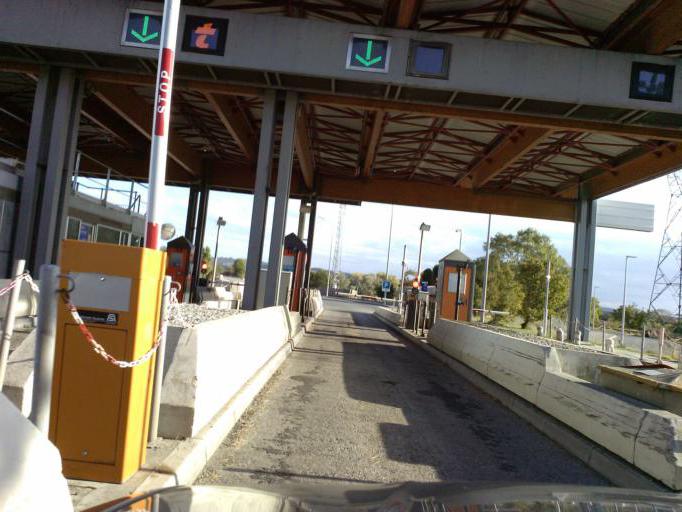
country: FR
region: Provence-Alpes-Cote d'Azur
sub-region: Departement des Alpes-de-Haute-Provence
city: Manosque
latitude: 43.8080
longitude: 5.8128
